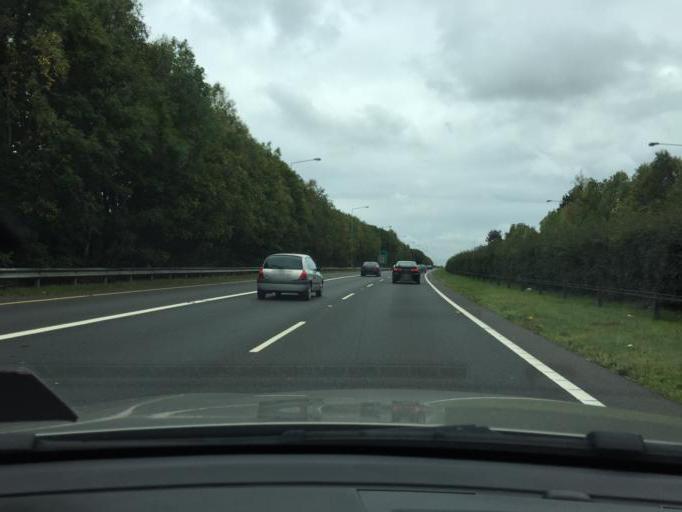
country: IE
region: Leinster
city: Hartstown
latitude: 53.4036
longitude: -6.4035
